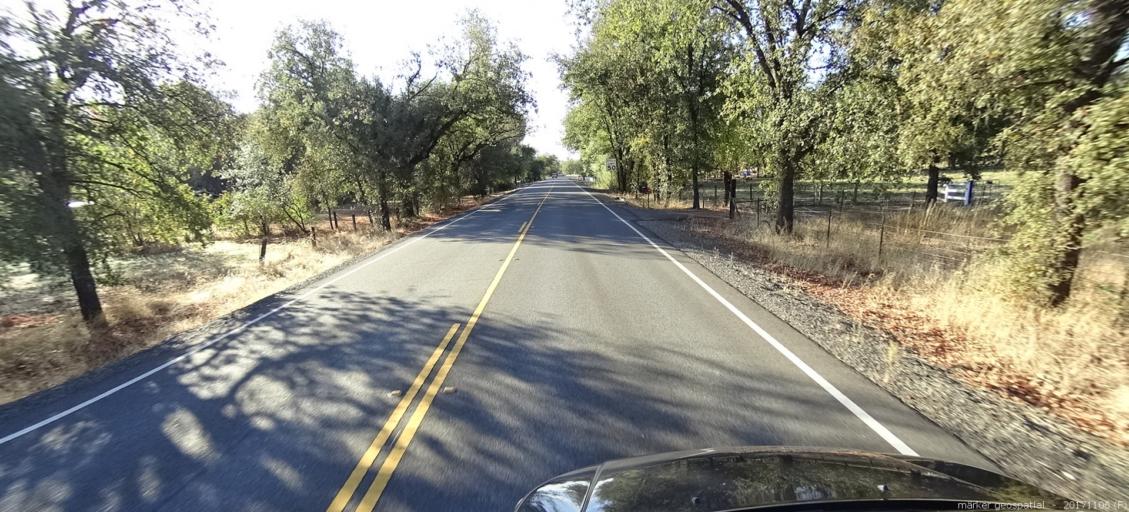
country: US
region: California
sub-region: Shasta County
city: Palo Cedro
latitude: 40.5997
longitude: -122.2346
